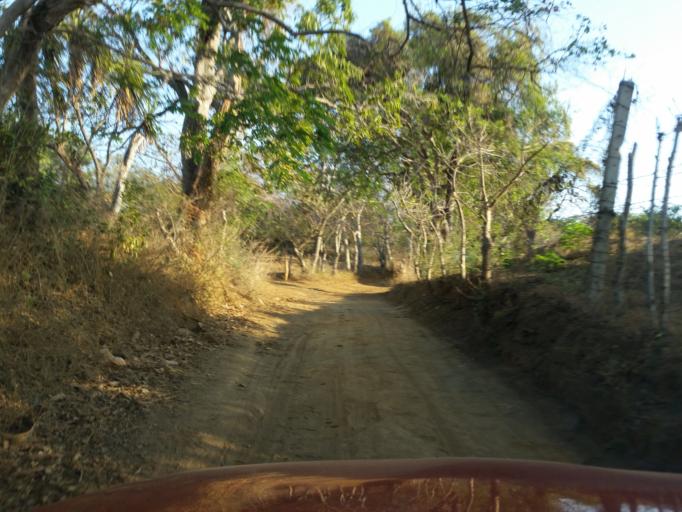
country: NI
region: Managua
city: Managua
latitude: 12.0767
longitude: -86.2582
